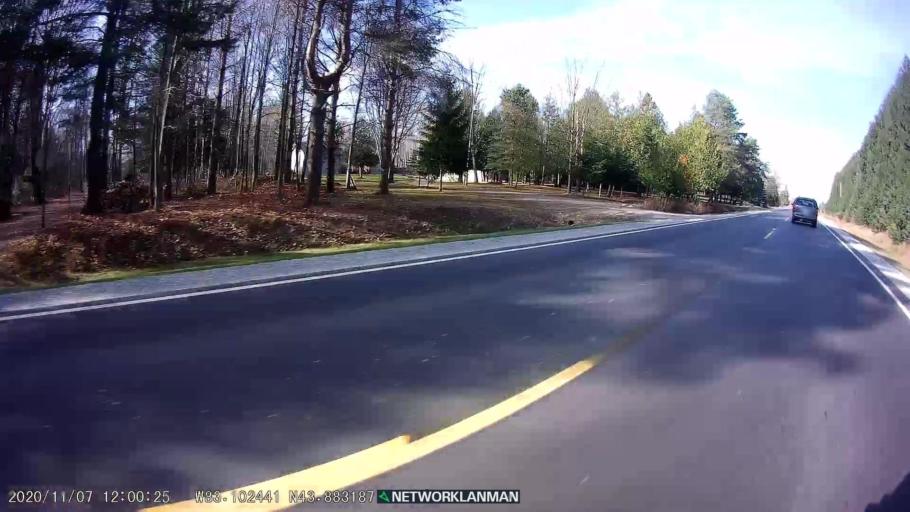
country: US
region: Michigan
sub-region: Huron County
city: Bad Axe
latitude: 43.8834
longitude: -83.1023
